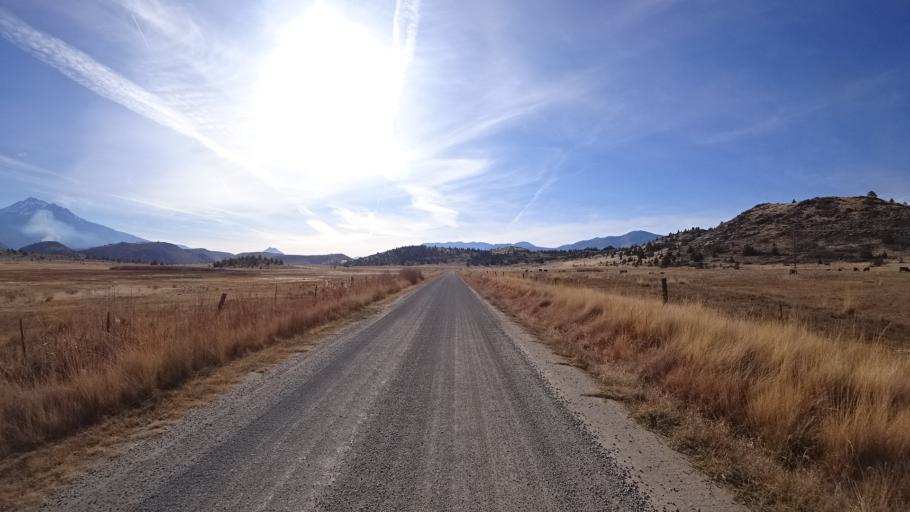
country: US
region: California
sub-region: Siskiyou County
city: Weed
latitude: 41.5451
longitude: -122.4726
